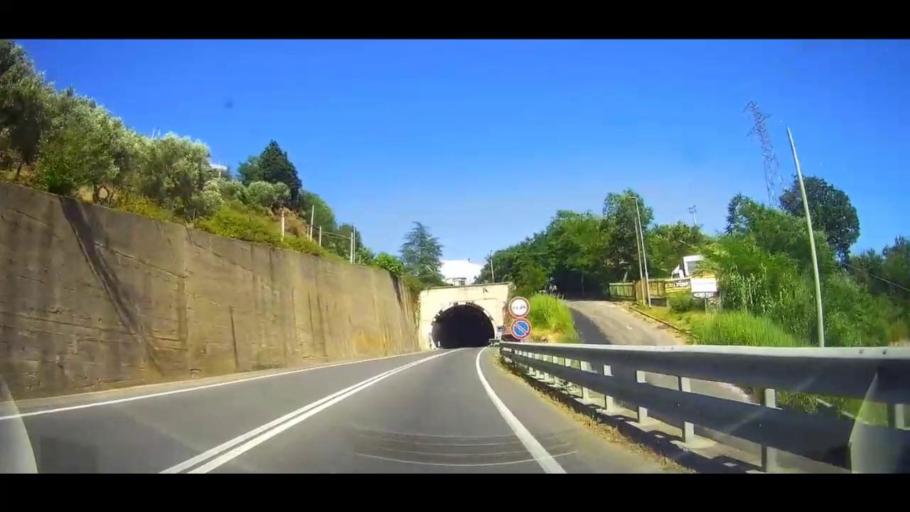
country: IT
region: Calabria
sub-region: Provincia di Cosenza
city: Cosenza
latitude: 39.2953
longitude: 16.2712
